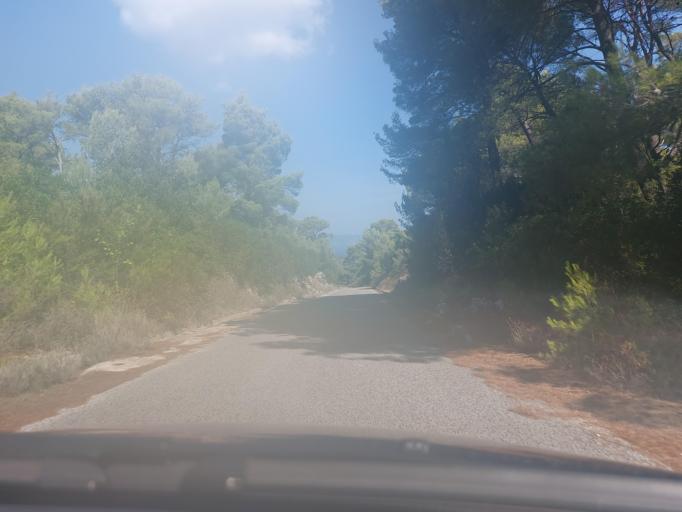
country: HR
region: Dubrovacko-Neretvanska
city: Smokvica
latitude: 42.7460
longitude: 16.8461
